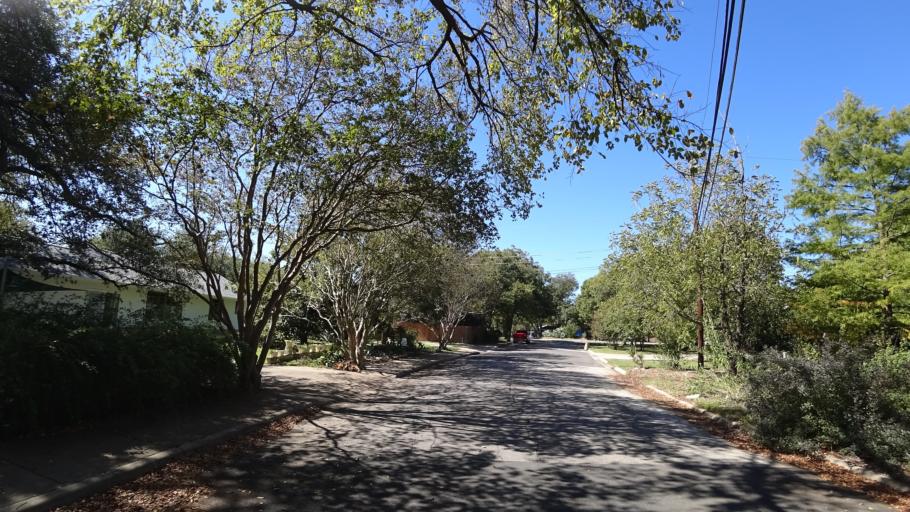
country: US
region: Texas
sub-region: Travis County
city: Austin
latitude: 30.3223
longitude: -97.7440
